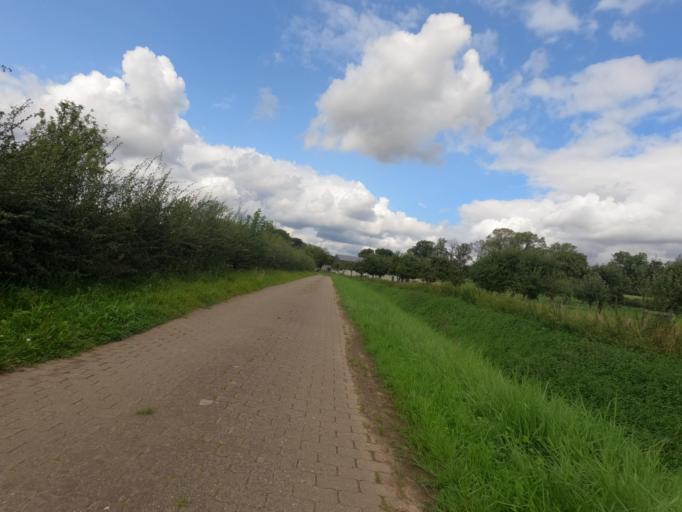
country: DE
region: North Rhine-Westphalia
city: Baesweiler
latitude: 50.9545
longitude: 6.2180
